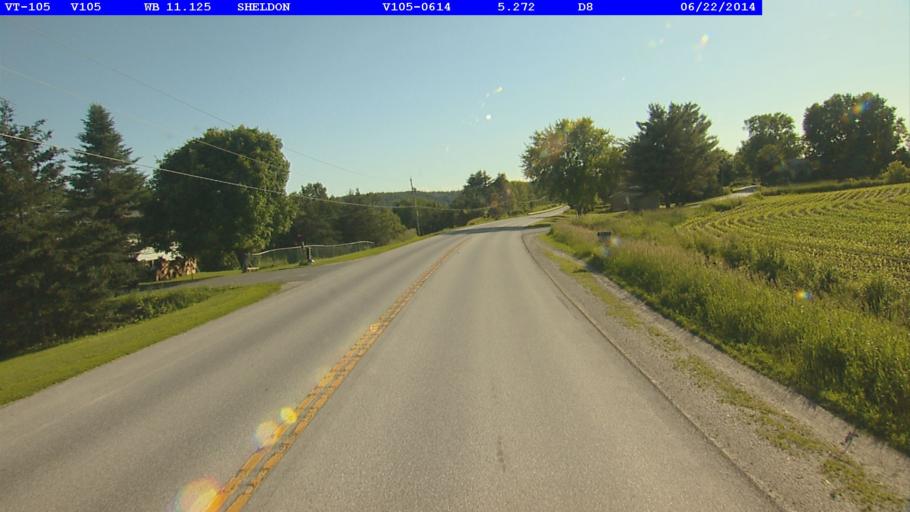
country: US
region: Vermont
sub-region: Franklin County
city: Enosburg Falls
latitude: 44.9018
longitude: -72.9298
